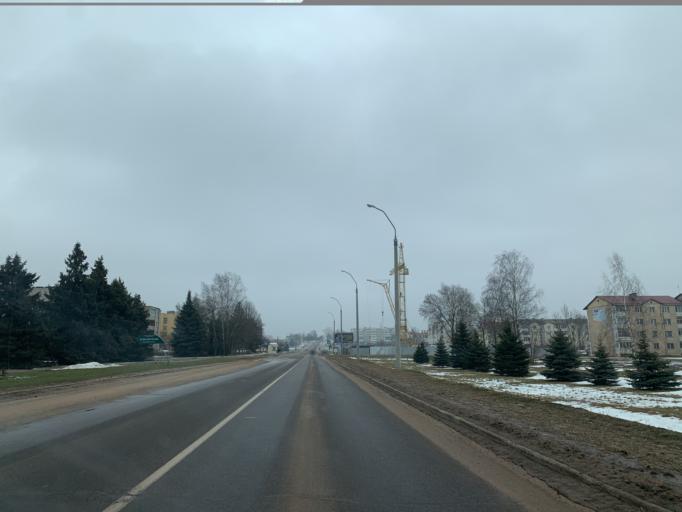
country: BY
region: Minsk
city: Nyasvizh
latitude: 53.2359
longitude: 26.6424
